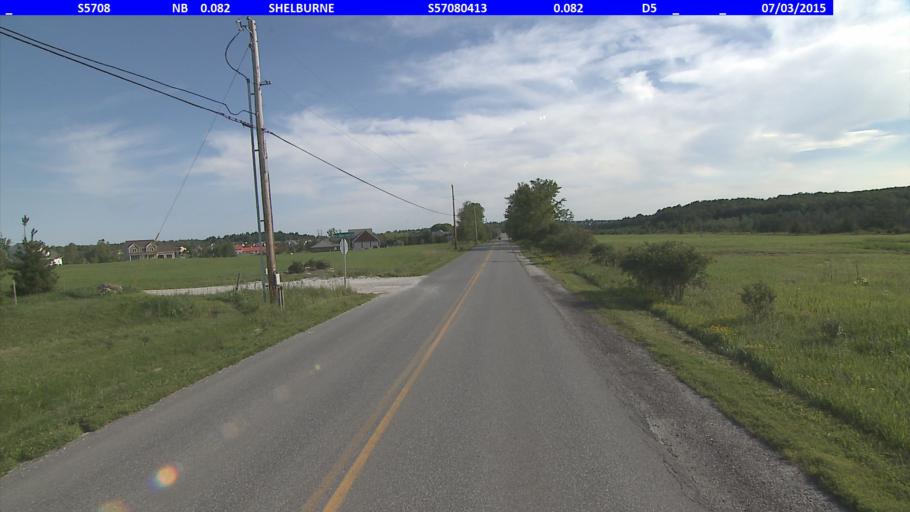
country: US
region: Vermont
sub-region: Chittenden County
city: South Burlington
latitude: 44.4087
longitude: -73.1778
